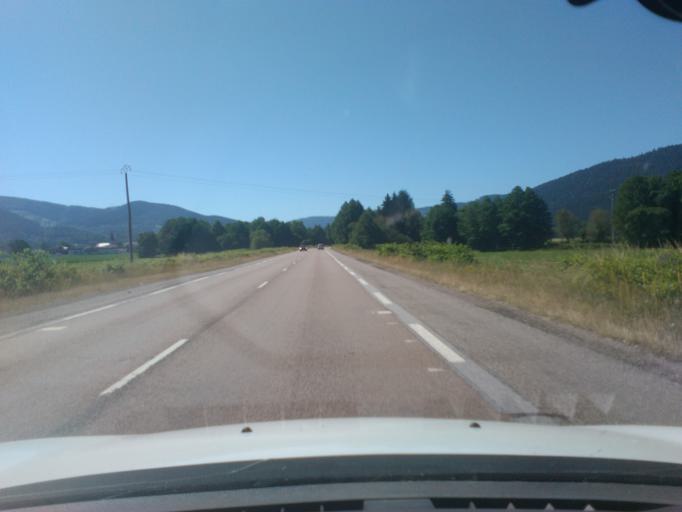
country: FR
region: Lorraine
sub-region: Departement des Vosges
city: Vagney
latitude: 48.0165
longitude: 6.7079
